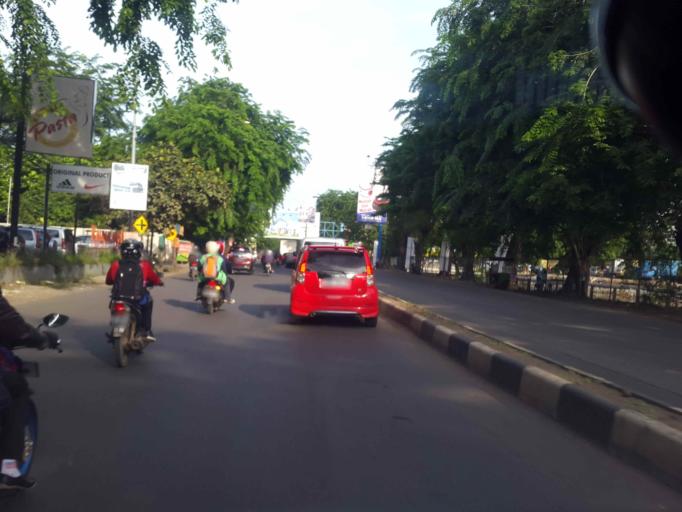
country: ID
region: West Java
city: Bekasi
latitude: -6.2492
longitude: 106.9668
